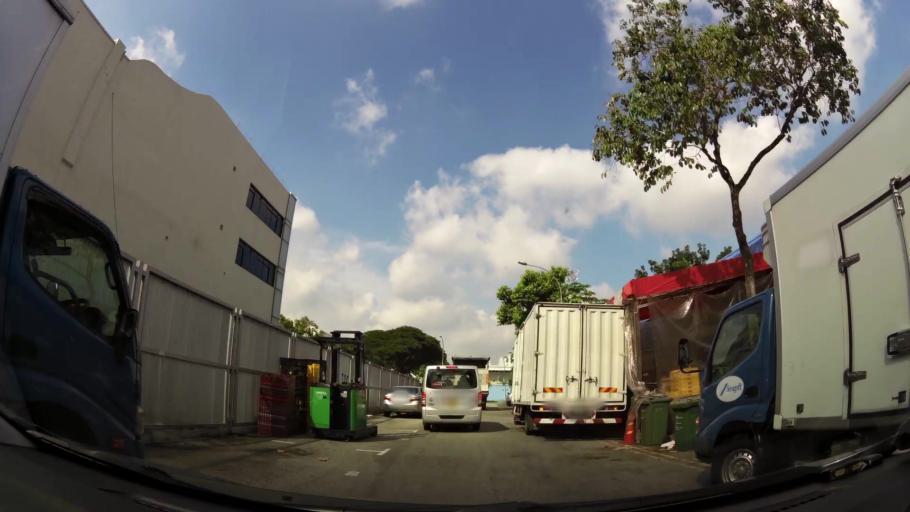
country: SG
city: Singapore
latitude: 1.3207
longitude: 103.8892
